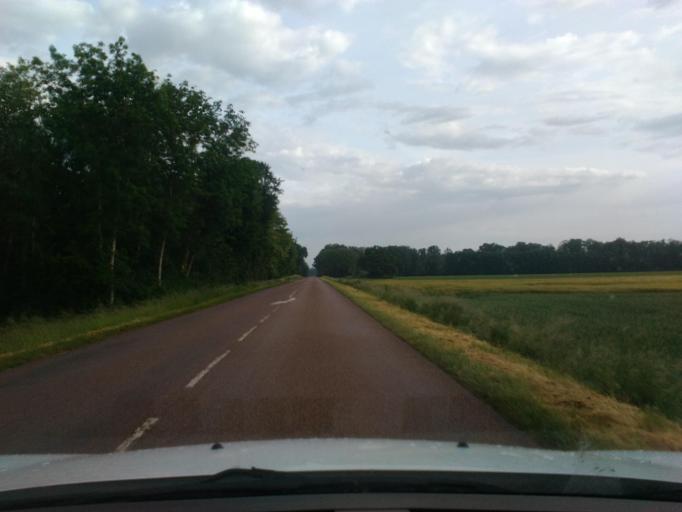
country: FR
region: Lorraine
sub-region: Departement des Vosges
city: Rambervillers
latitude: 48.4178
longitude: 6.5849
